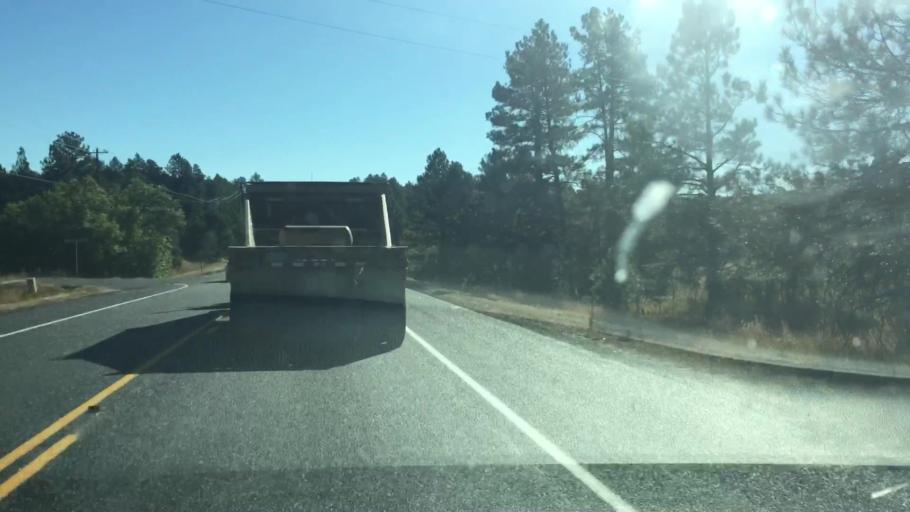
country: US
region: Colorado
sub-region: Elbert County
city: Ponderosa Park
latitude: 39.3789
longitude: -104.7087
